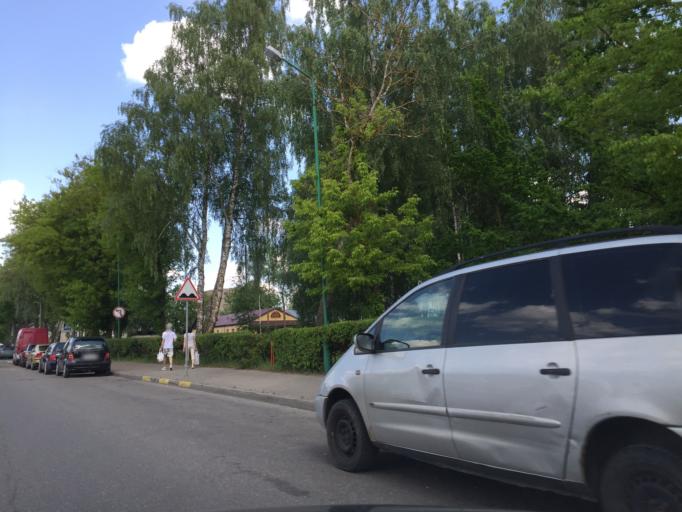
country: LT
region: Klaipedos apskritis
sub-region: Klaipeda
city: Palanga
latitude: 55.9174
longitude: 21.0716
